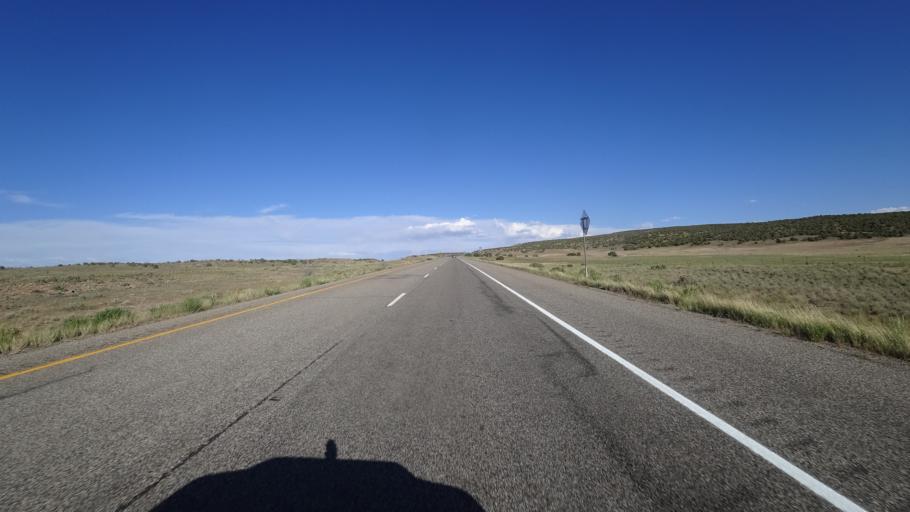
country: US
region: Colorado
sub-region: Mesa County
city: Loma
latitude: 39.1916
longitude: -109.0468
